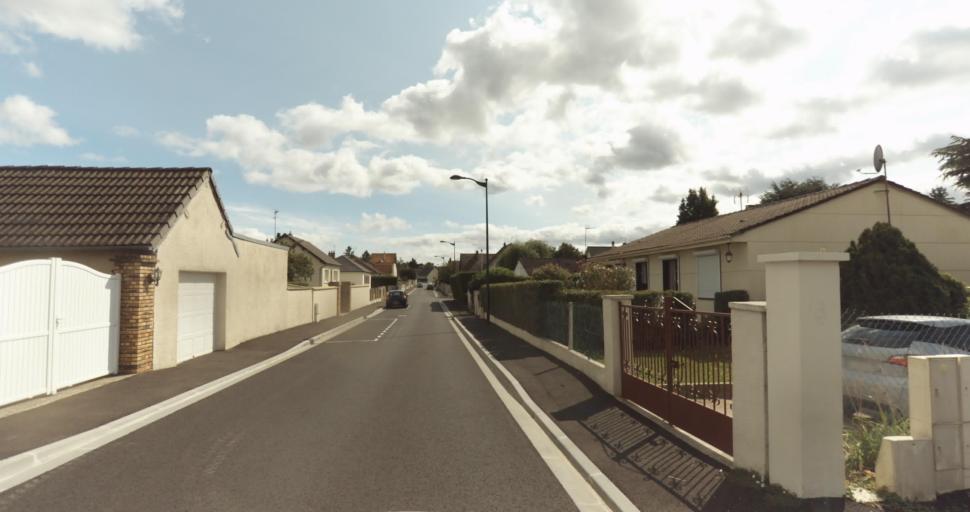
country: FR
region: Haute-Normandie
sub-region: Departement de l'Eure
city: La Couture-Boussey
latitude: 48.8971
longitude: 1.4019
